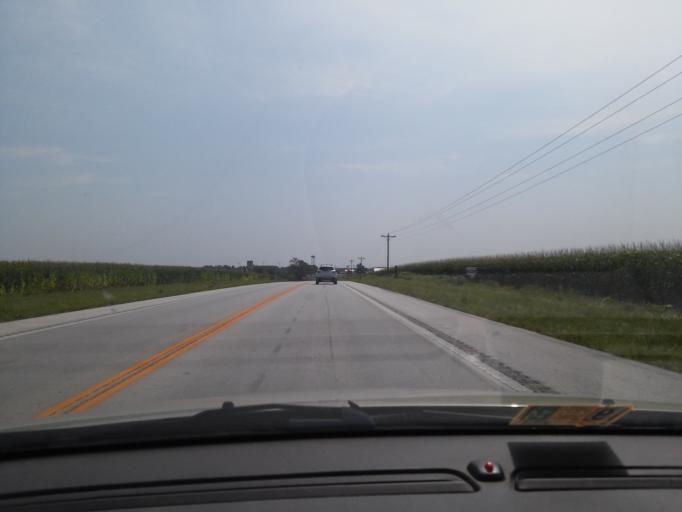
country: US
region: Missouri
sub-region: Montgomery County
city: Wellsville
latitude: 39.1630
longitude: -91.6562
